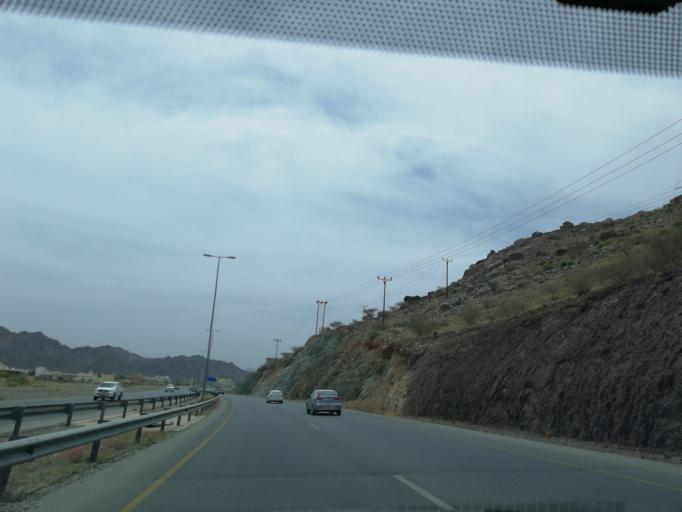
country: OM
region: Muhafazat ad Dakhiliyah
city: Izki
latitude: 23.1443
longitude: 57.8419
